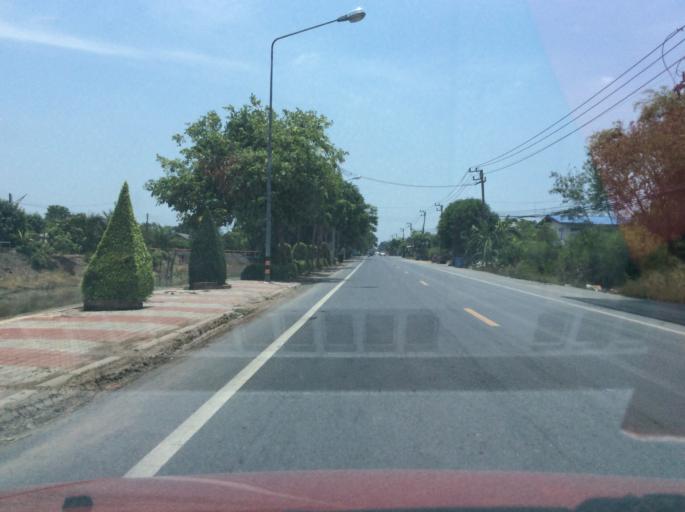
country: TH
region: Pathum Thani
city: Lam Luk Ka
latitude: 13.9553
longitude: 100.7274
